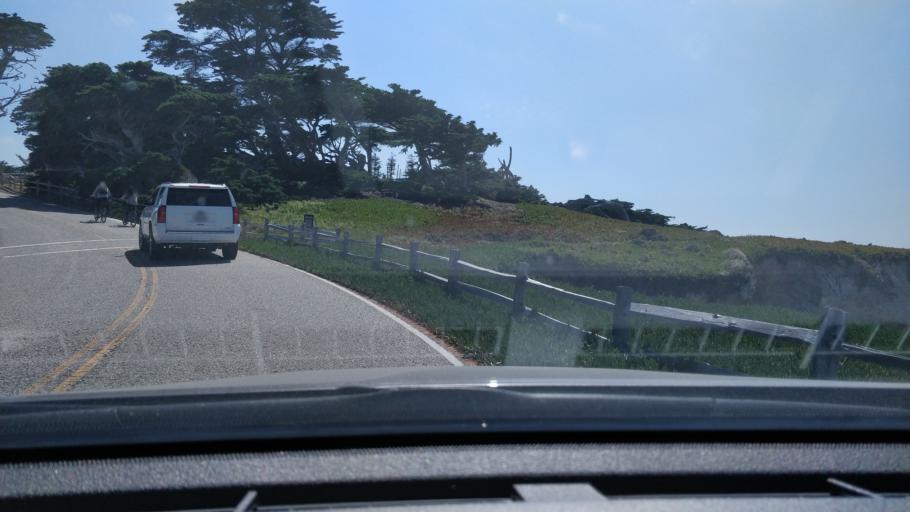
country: US
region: California
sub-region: Monterey County
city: Del Monte Forest
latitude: 36.5830
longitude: -121.9733
